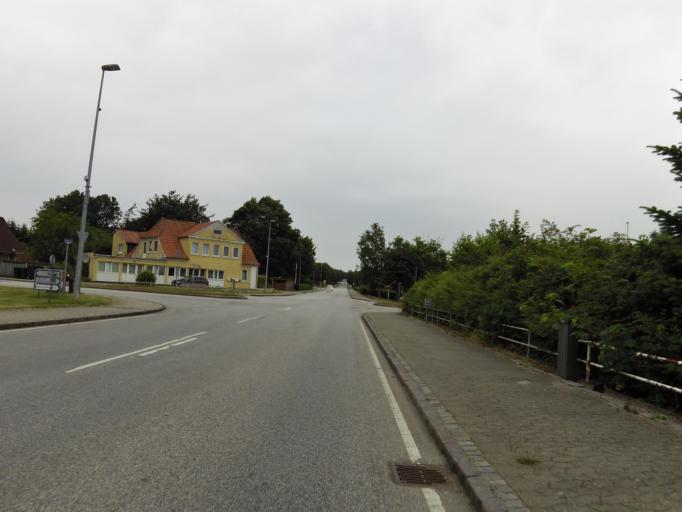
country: DK
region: South Denmark
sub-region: Tonder Kommune
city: Logumkloster
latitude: 55.1501
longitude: 8.9608
